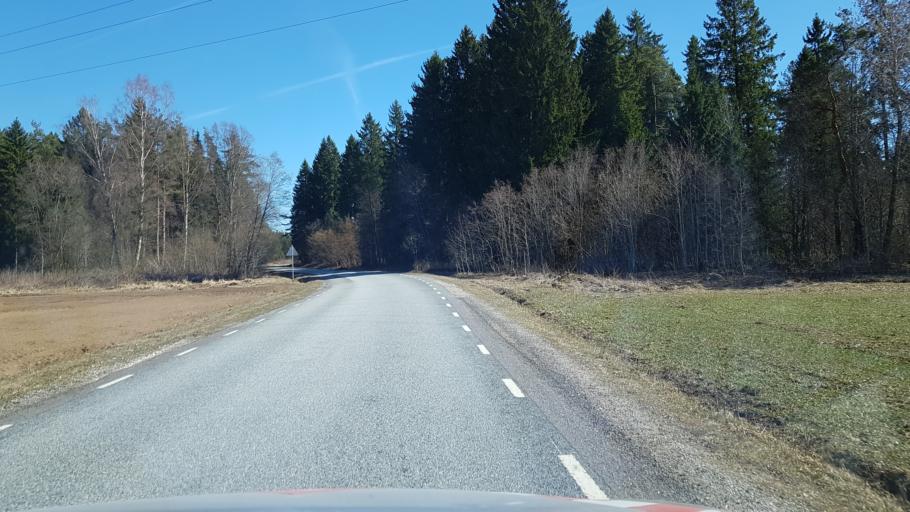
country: EE
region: Laeaene-Virumaa
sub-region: Someru vald
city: Someru
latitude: 59.3326
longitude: 26.5498
